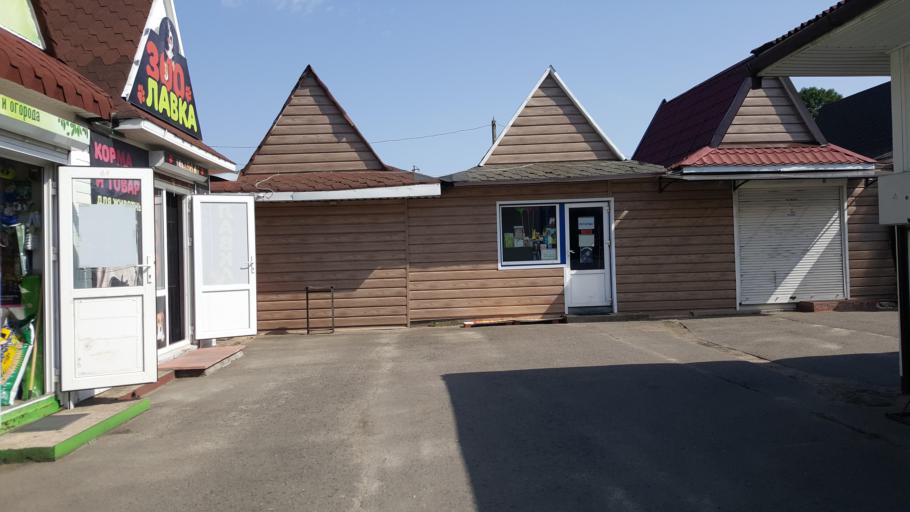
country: BY
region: Brest
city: Zhabinka
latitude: 52.1993
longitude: 24.0192
